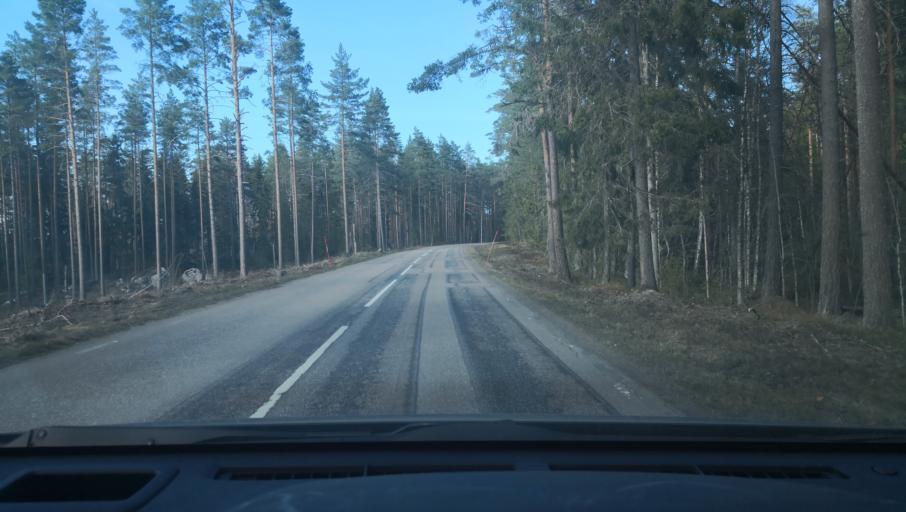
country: SE
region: Uppsala
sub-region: Heby Kommun
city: Morgongava
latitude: 60.0028
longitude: 16.9315
